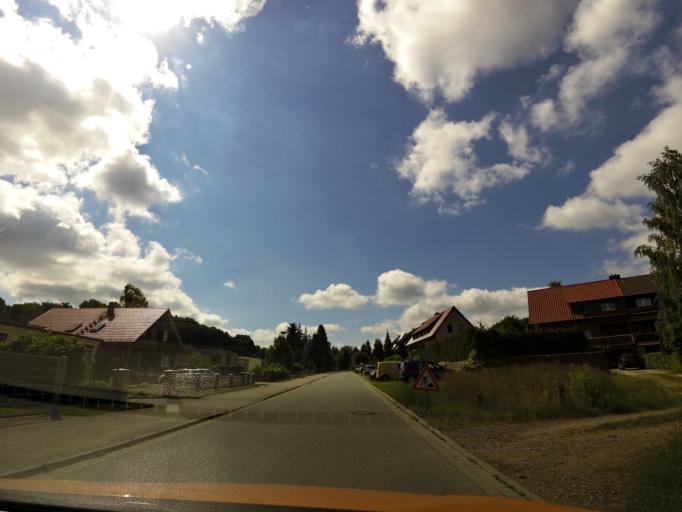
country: DE
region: Mecklenburg-Vorpommern
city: Plau am See
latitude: 53.4431
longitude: 12.2836
